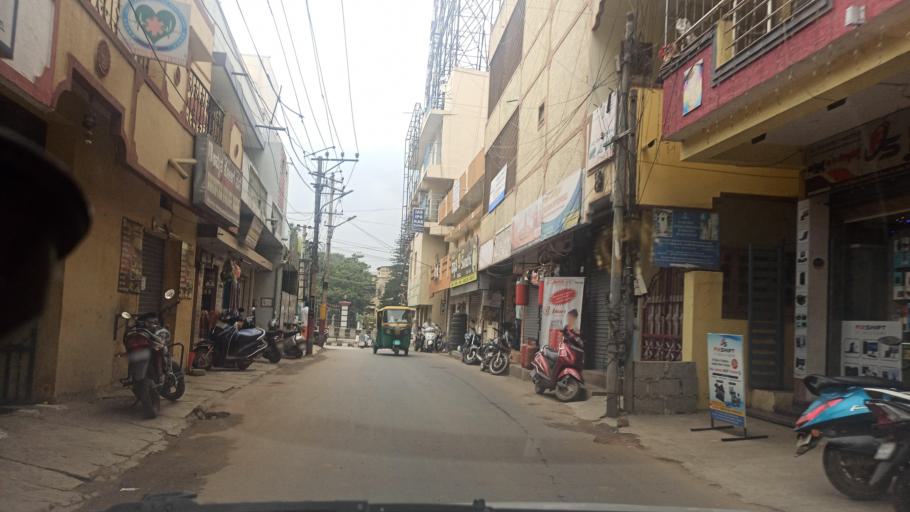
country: IN
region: Karnataka
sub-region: Bangalore Urban
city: Yelahanka
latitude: 13.0374
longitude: 77.5901
